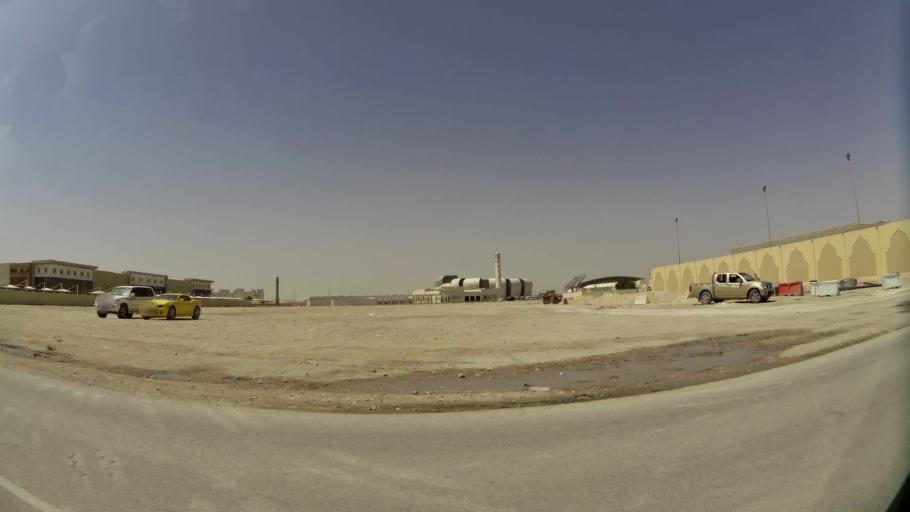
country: QA
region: Baladiyat Umm Salal
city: Umm Salal Muhammad
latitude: 25.3705
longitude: 51.4756
